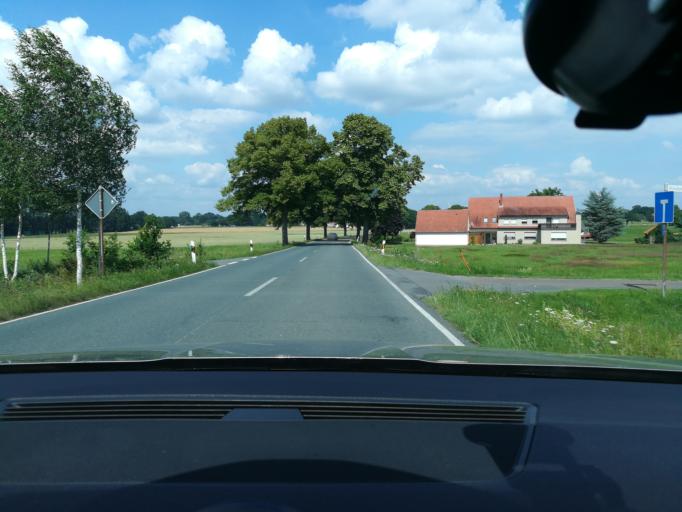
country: DE
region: North Rhine-Westphalia
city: Espelkamp
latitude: 52.3508
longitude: 8.6566
